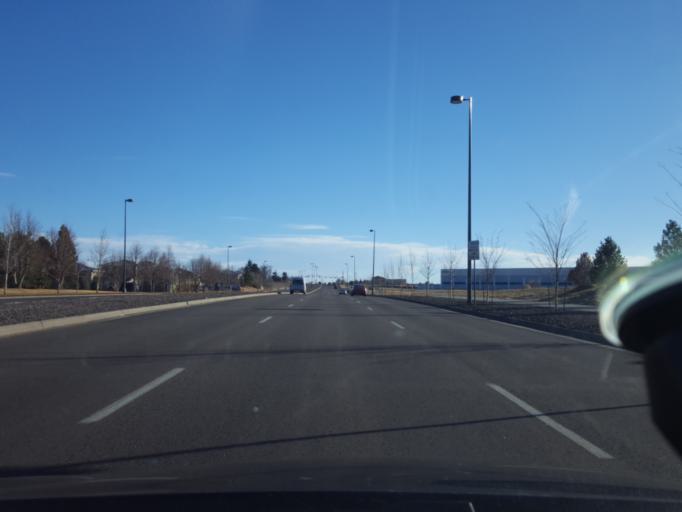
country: US
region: Colorado
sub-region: Adams County
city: Aurora
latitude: 39.7744
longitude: -104.7723
